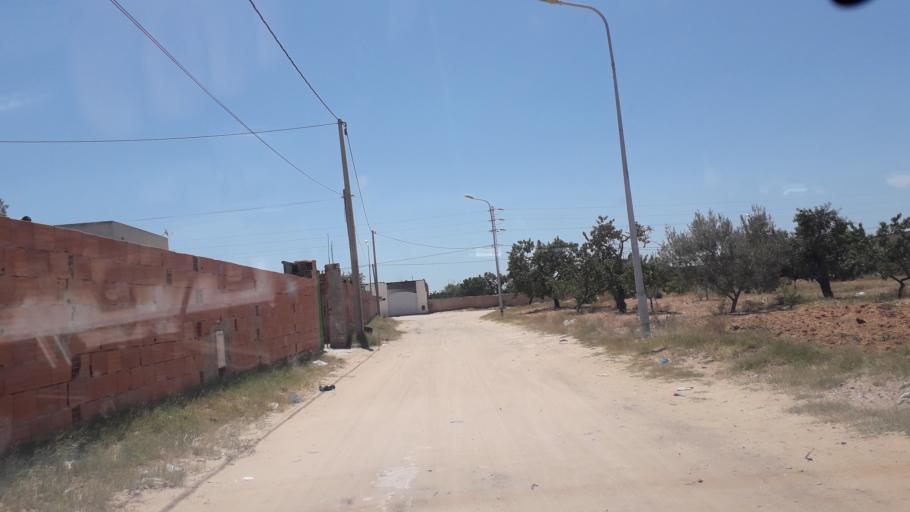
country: TN
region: Safaqis
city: Al Qarmadah
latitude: 34.8287
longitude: 10.7731
